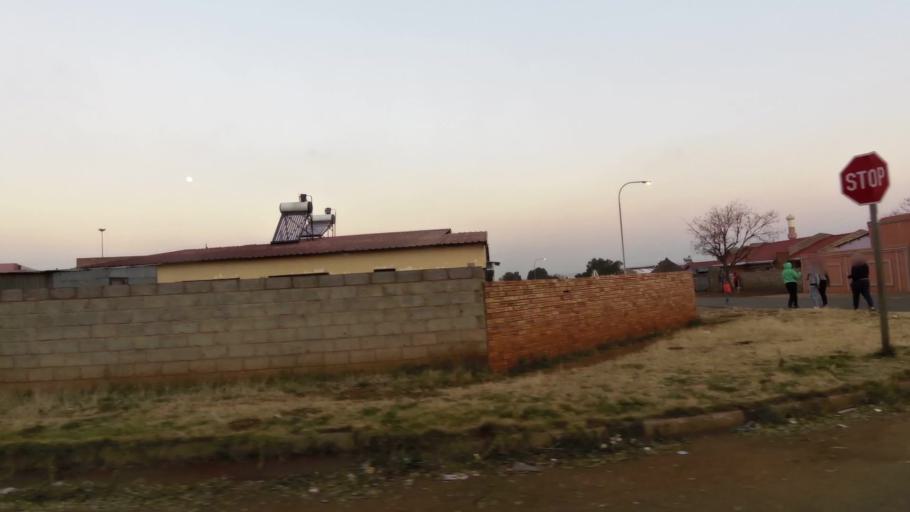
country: ZA
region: Gauteng
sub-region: City of Johannesburg Metropolitan Municipality
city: Soweto
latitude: -26.2910
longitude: 27.8755
